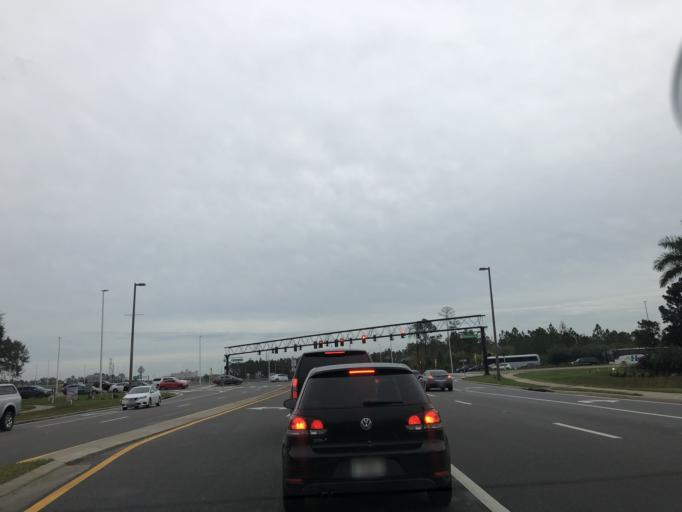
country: US
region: Florida
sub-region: Orange County
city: Williamsburg
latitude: 28.4193
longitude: -81.4609
